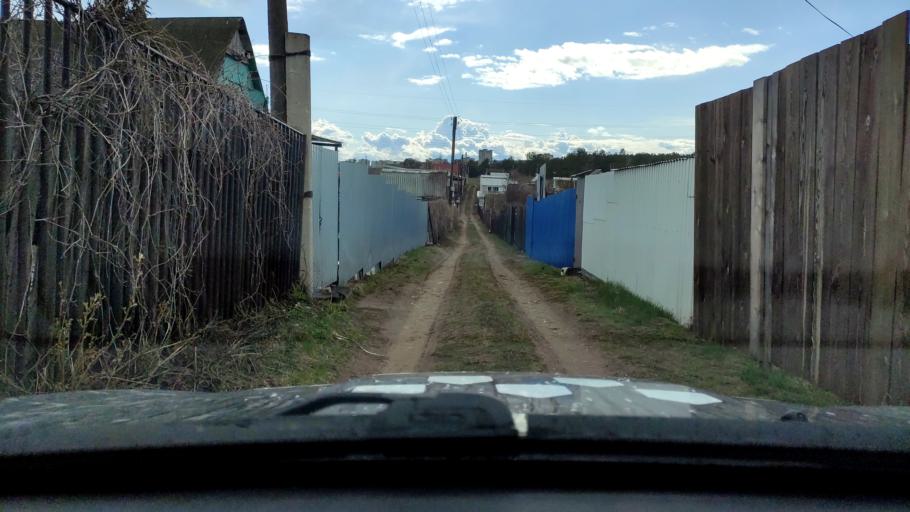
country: RU
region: Samara
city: Zhigulevsk
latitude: 53.4954
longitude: 49.4941
